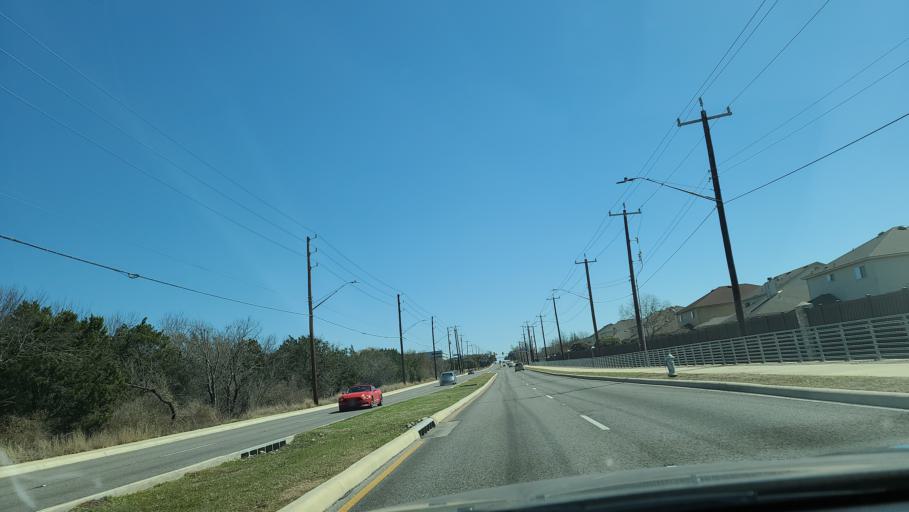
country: US
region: Texas
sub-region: Bexar County
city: Shavano Park
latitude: 29.5723
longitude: -98.6043
